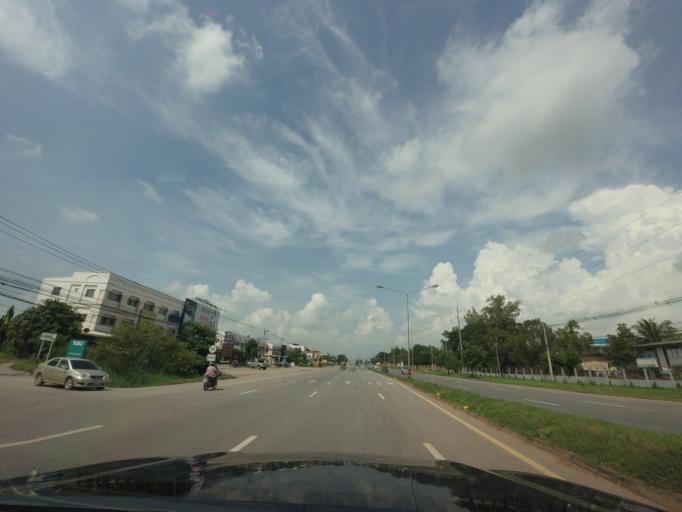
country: TH
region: Khon Kaen
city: Ban Fang
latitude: 16.4503
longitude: 102.7290
